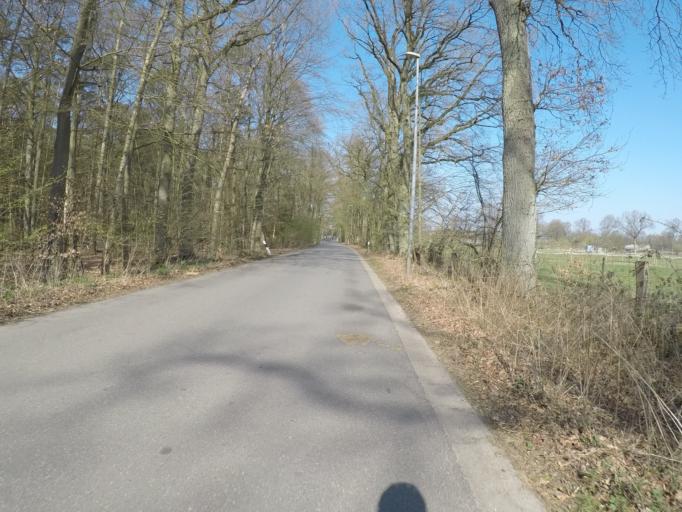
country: DE
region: Schleswig-Holstein
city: Rellingen
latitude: 53.6088
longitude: 9.7981
